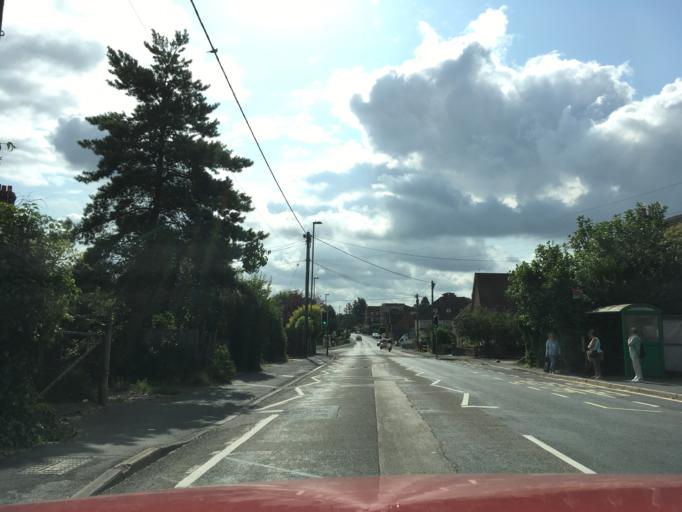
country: GB
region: England
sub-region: Hampshire
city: Bishops Waltham
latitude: 50.9563
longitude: -1.2237
